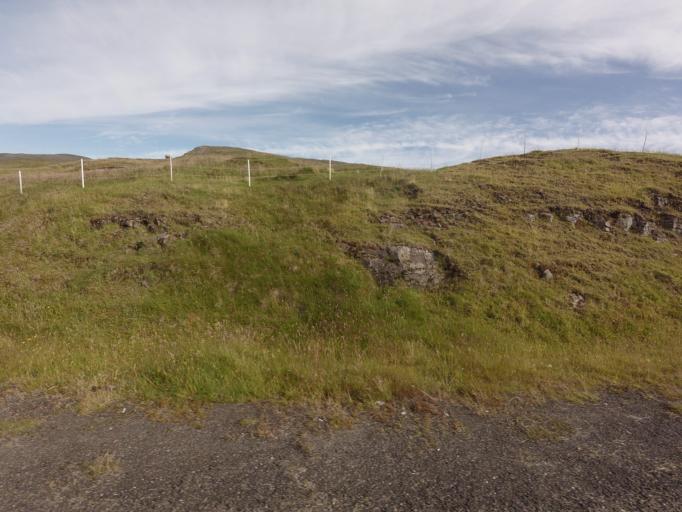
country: FO
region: Vagar
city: Sorvagur
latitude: 62.0690
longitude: -7.2890
